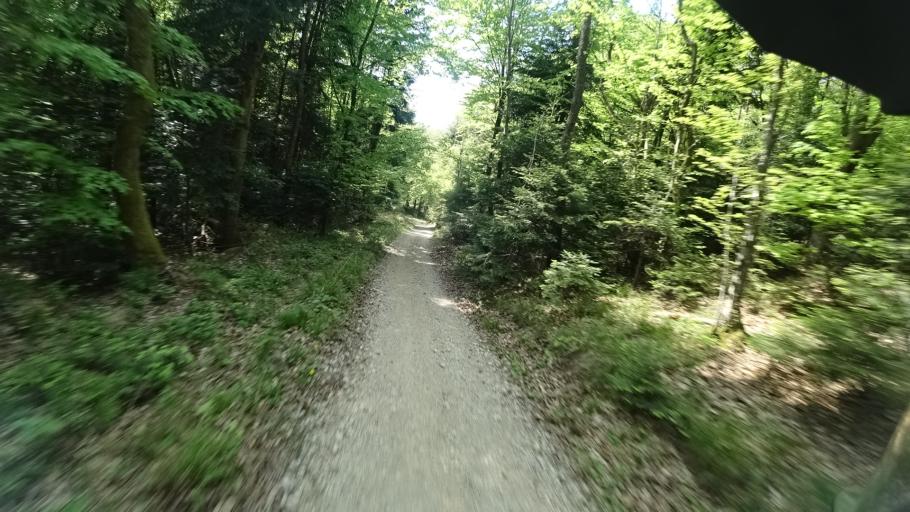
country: HR
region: Grad Zagreb
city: Kasina
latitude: 45.9420
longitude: 16.0279
